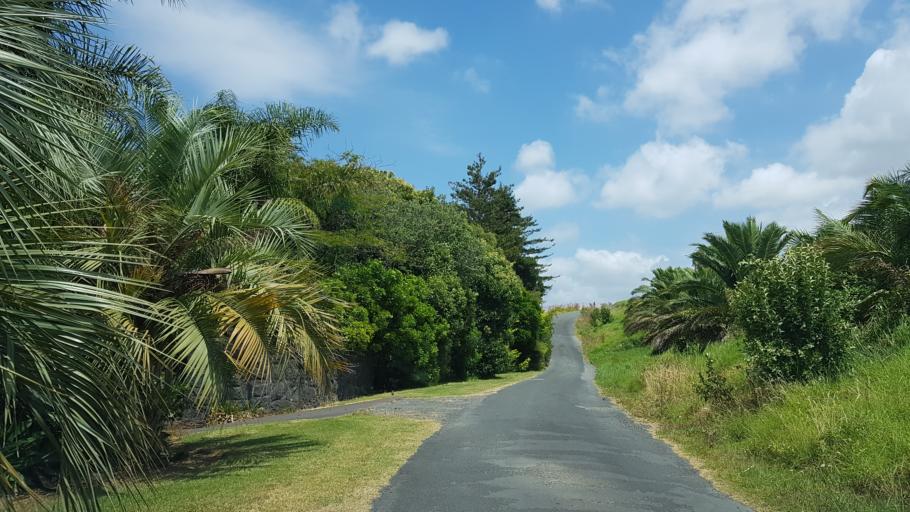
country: NZ
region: Auckland
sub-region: Auckland
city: Rosebank
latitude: -36.8045
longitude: 174.6699
